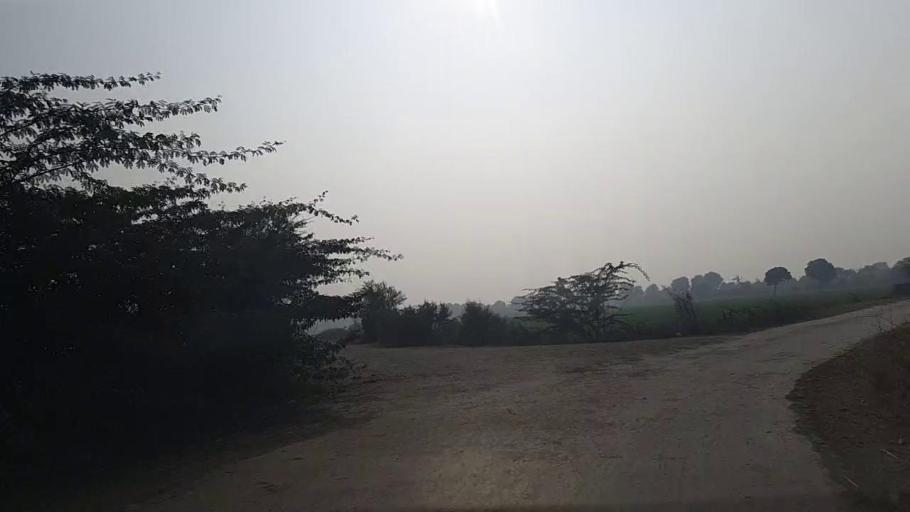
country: PK
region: Sindh
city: Sanghar
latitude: 26.0758
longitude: 68.8745
